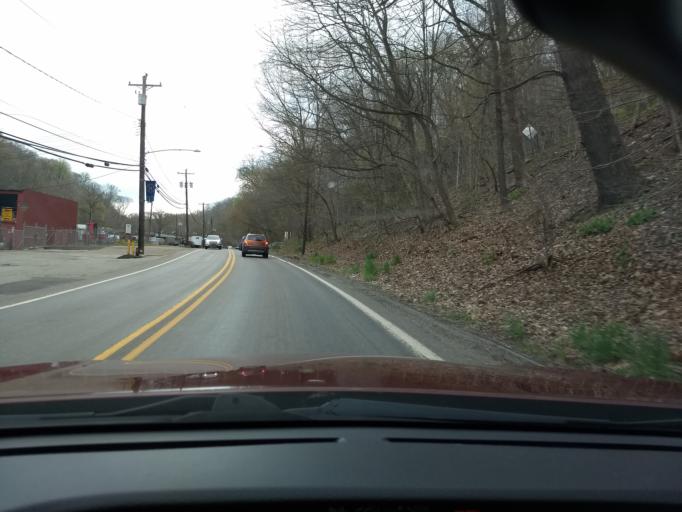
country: US
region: Pennsylvania
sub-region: Allegheny County
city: Turtle Creek
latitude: 40.4287
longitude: -79.8154
